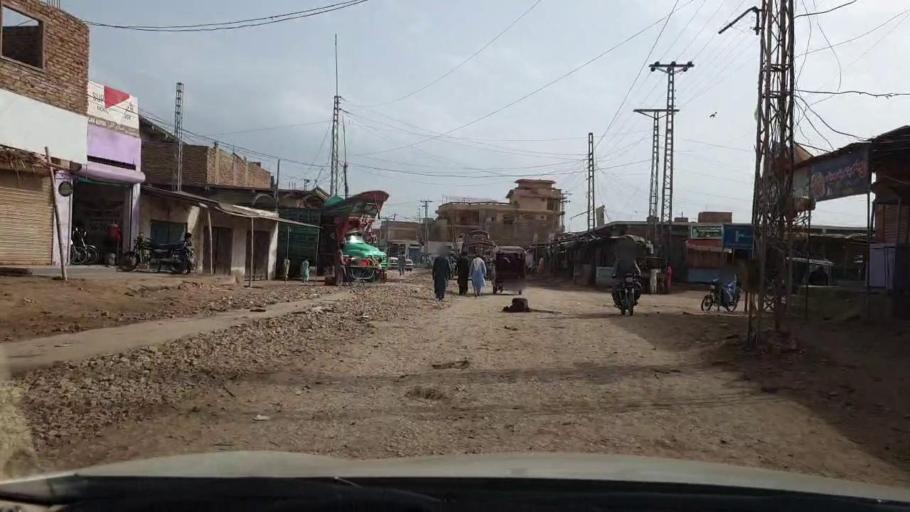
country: PK
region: Sindh
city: Matli
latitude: 25.0388
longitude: 68.6613
